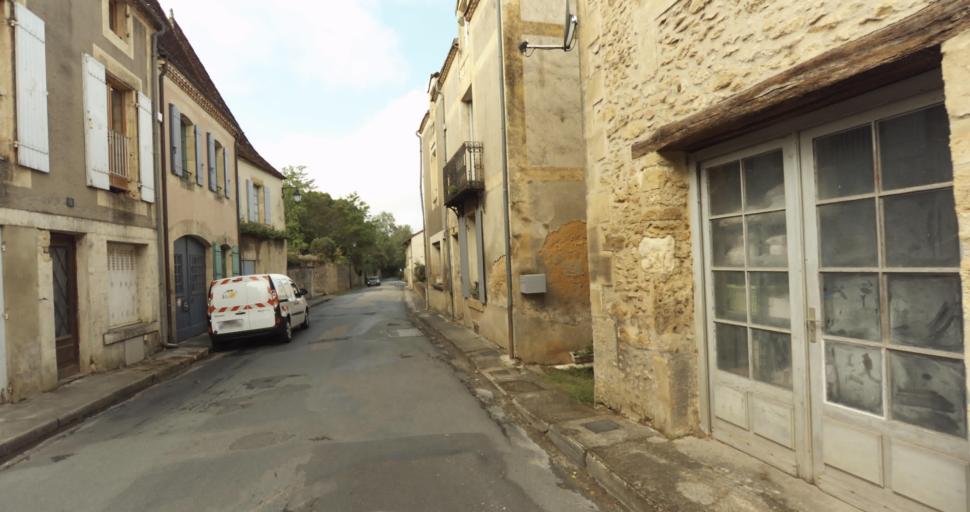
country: FR
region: Aquitaine
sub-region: Departement de la Dordogne
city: Vergt
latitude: 44.9460
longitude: 0.8079
